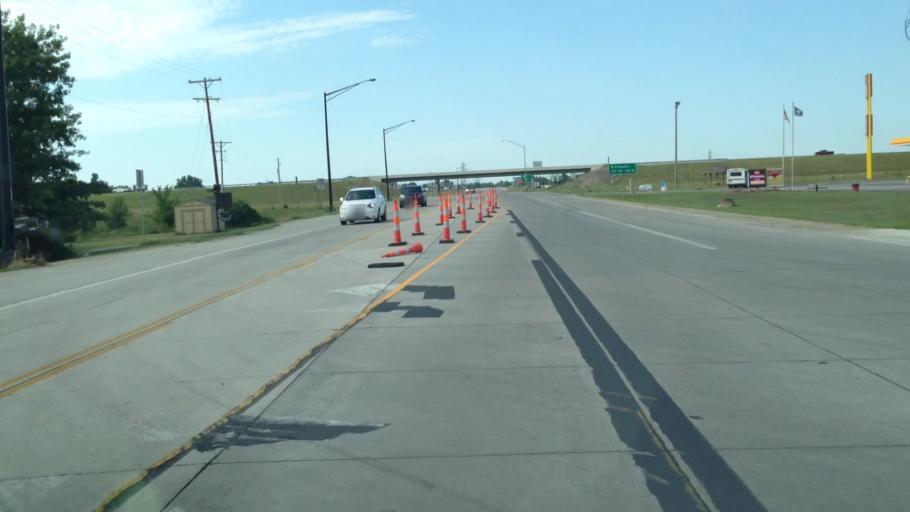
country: US
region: Kansas
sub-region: Labette County
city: Parsons
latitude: 37.3637
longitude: -95.2586
